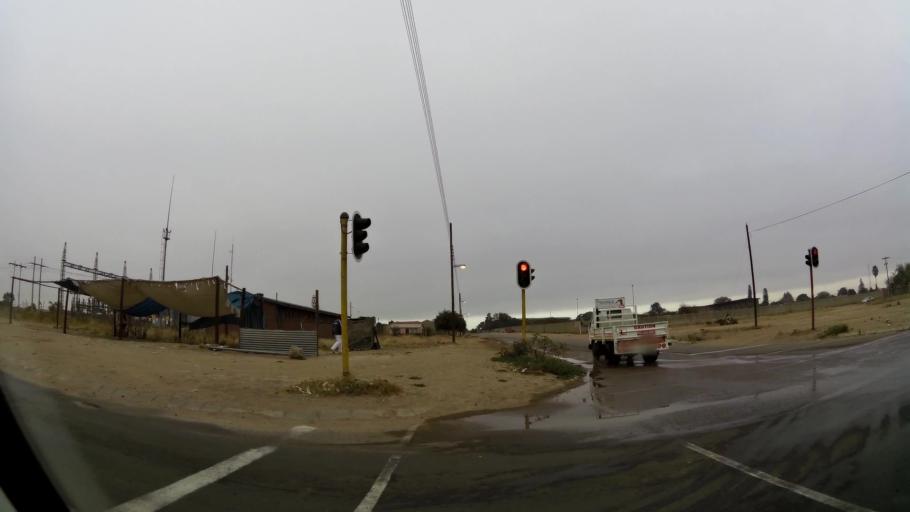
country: ZA
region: Limpopo
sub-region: Capricorn District Municipality
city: Polokwane
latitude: -23.8374
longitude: 29.3955
